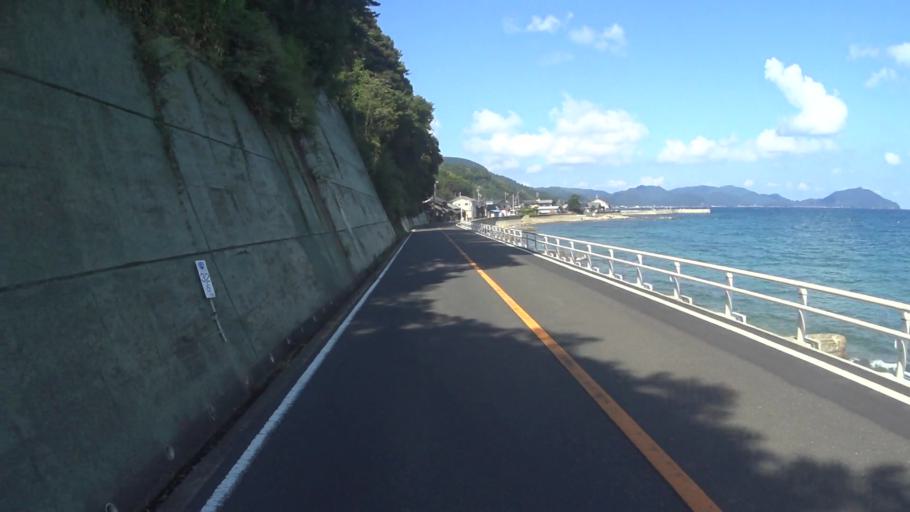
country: JP
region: Kyoto
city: Miyazu
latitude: 35.6223
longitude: 135.2450
